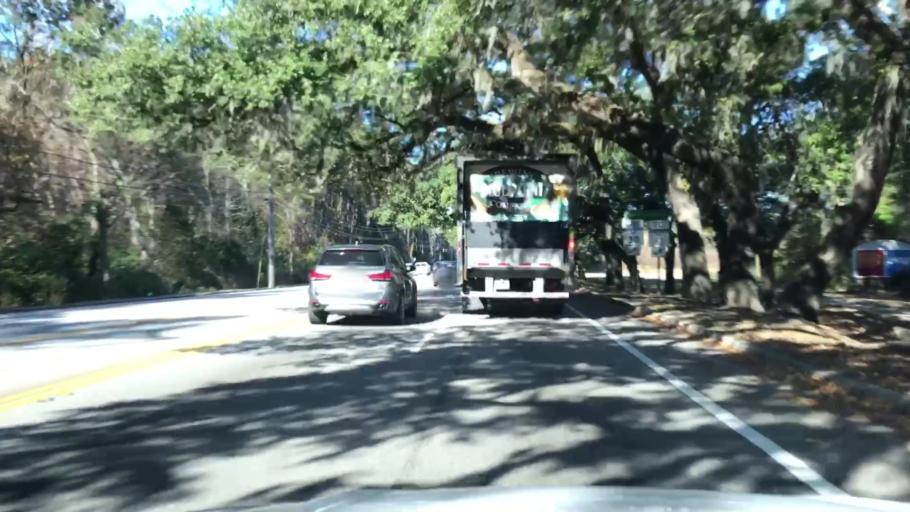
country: US
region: South Carolina
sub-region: Charleston County
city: Charleston
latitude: 32.7472
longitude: -79.9708
